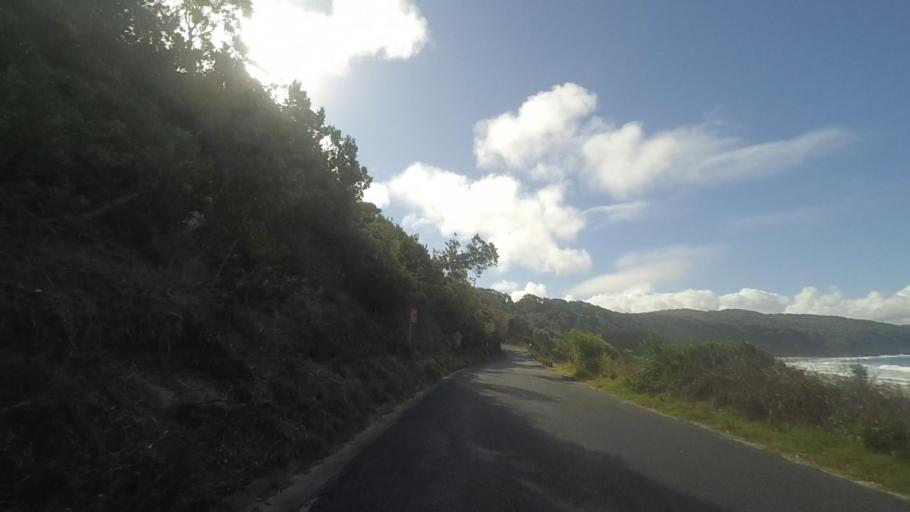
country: AU
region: New South Wales
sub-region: Great Lakes
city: Forster
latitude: -32.4321
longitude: 152.5225
